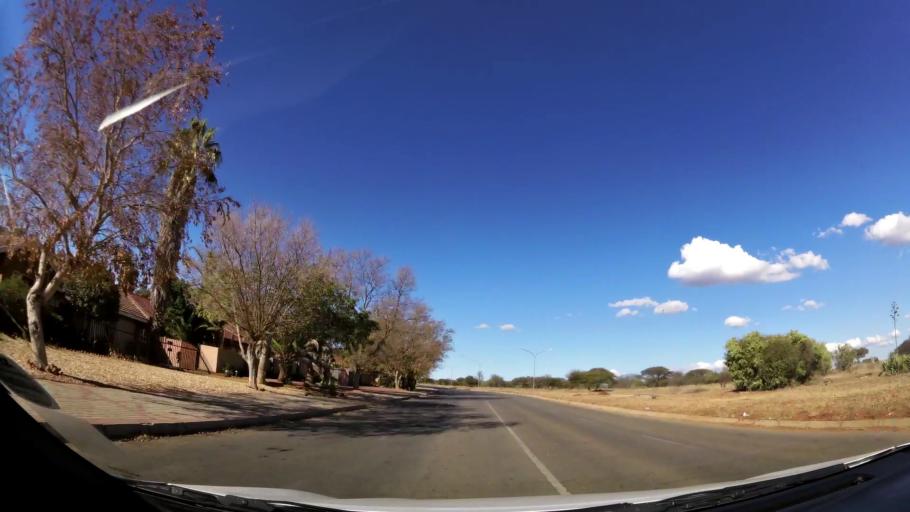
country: ZA
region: Limpopo
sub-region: Capricorn District Municipality
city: Polokwane
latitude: -23.9177
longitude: 29.4837
